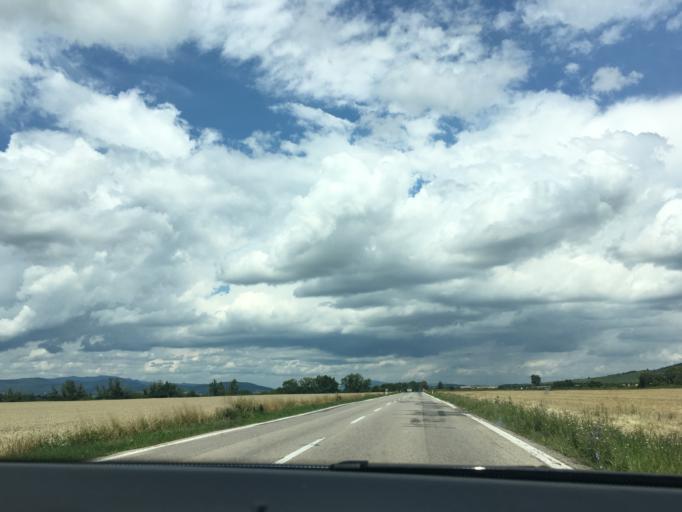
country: HU
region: Borsod-Abauj-Zemplen
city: Satoraljaujhely
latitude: 48.4372
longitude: 21.6563
